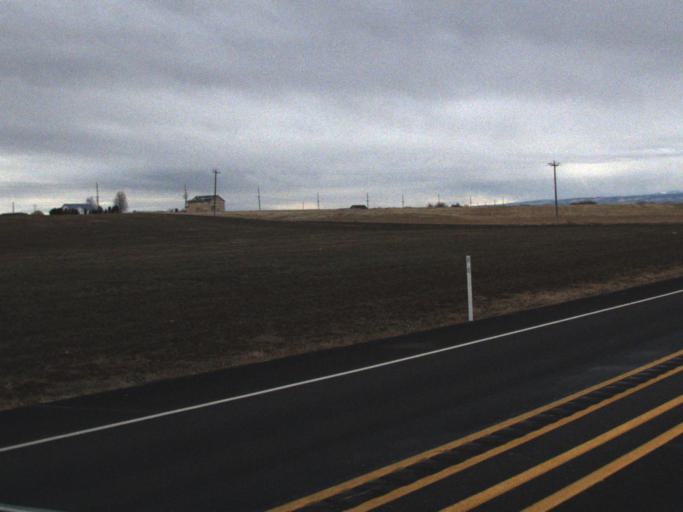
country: US
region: Washington
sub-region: Walla Walla County
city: Garrett
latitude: 46.0394
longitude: -118.6610
